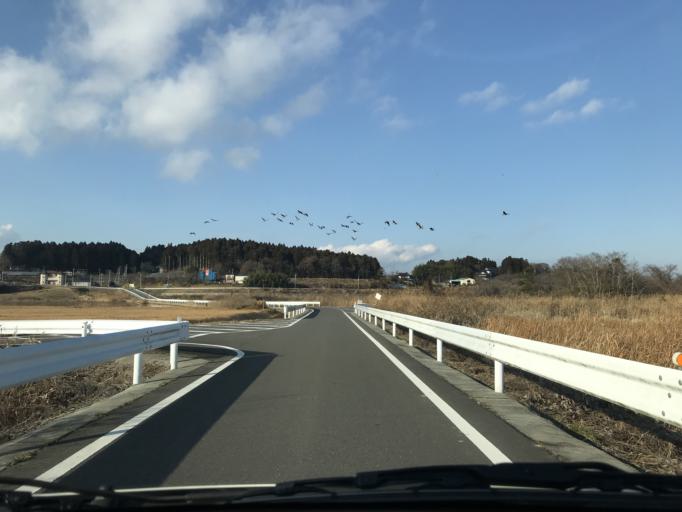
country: JP
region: Miyagi
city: Wakuya
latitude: 38.6810
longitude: 141.1162
